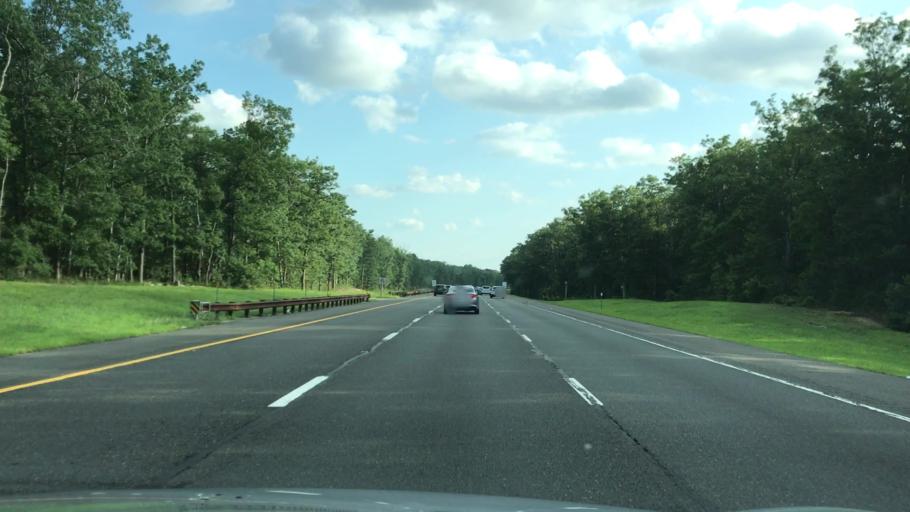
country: US
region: New Jersey
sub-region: Ocean County
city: Ocean Acres
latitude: 39.7441
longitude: -74.2577
